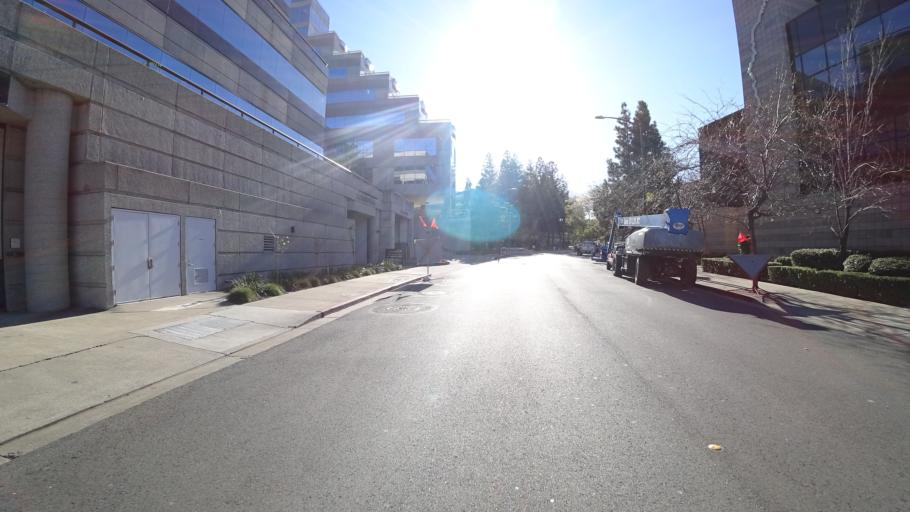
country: US
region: California
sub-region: Contra Costa County
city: Walnut Creek
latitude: 37.9095
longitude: -122.0671
